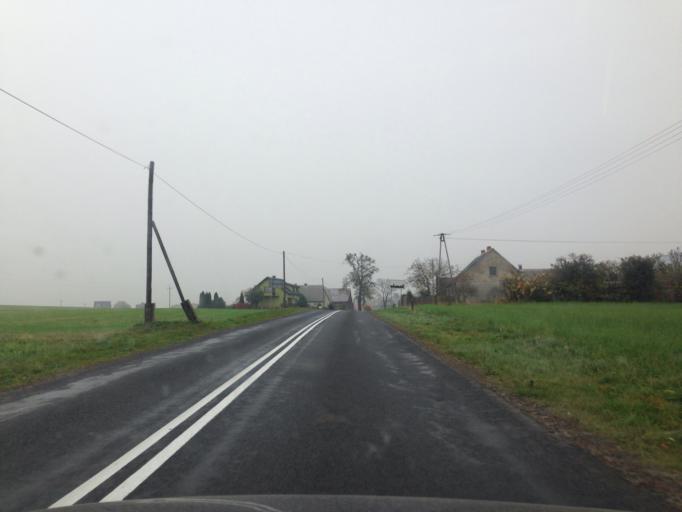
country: PL
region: Kujawsko-Pomorskie
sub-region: Powiat brodnicki
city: Bartniczka
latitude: 53.2497
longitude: 19.5596
